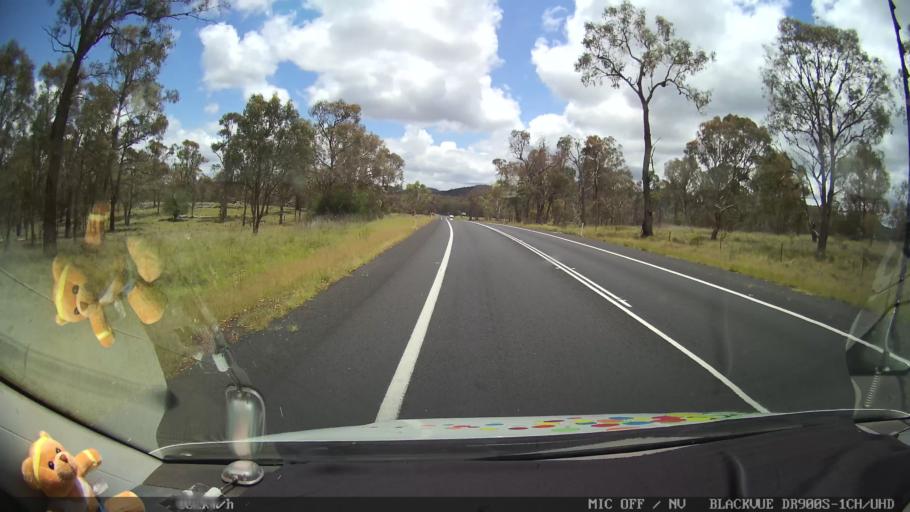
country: AU
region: New South Wales
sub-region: Glen Innes Severn
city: Glen Innes
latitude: -29.3653
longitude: 151.8988
